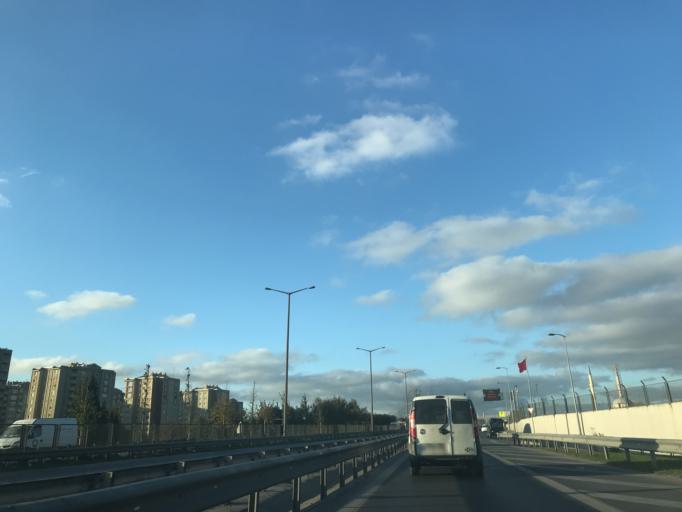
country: TR
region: Istanbul
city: Esenler
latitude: 41.0464
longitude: 28.8850
